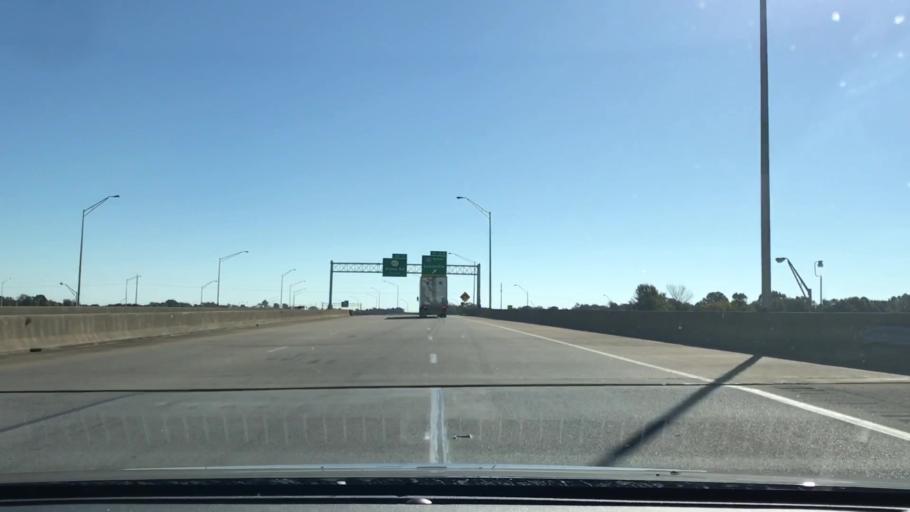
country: US
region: Kentucky
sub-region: Warren County
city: Plano
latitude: 36.9104
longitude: -86.4329
